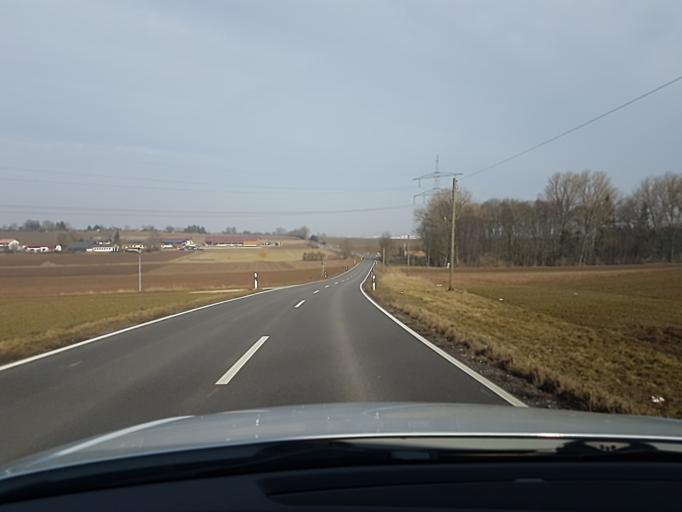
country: DE
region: Baden-Wuerttemberg
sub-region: Regierungsbezirk Stuttgart
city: Nordheim
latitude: 49.1273
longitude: 9.1299
